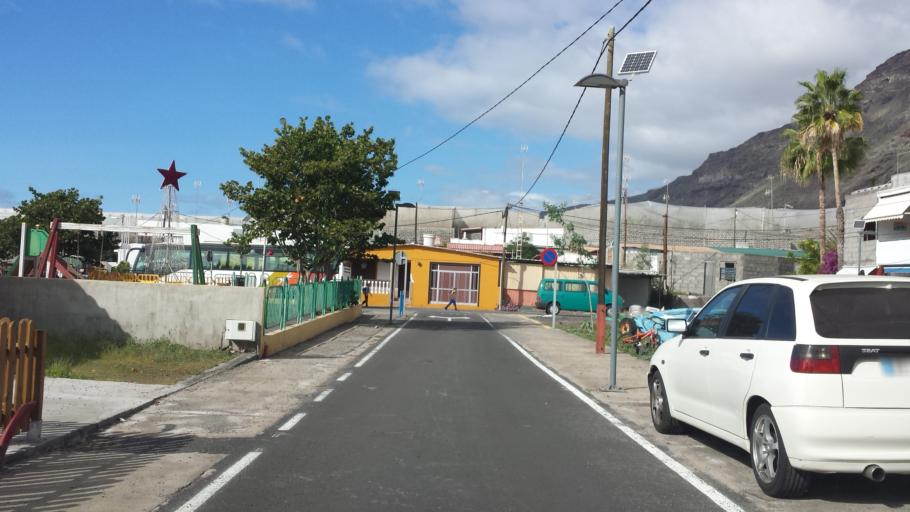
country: ES
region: Canary Islands
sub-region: Provincia de Santa Cruz de Tenerife
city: Fuencaliente de la Palma
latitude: 28.5533
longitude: -17.8888
